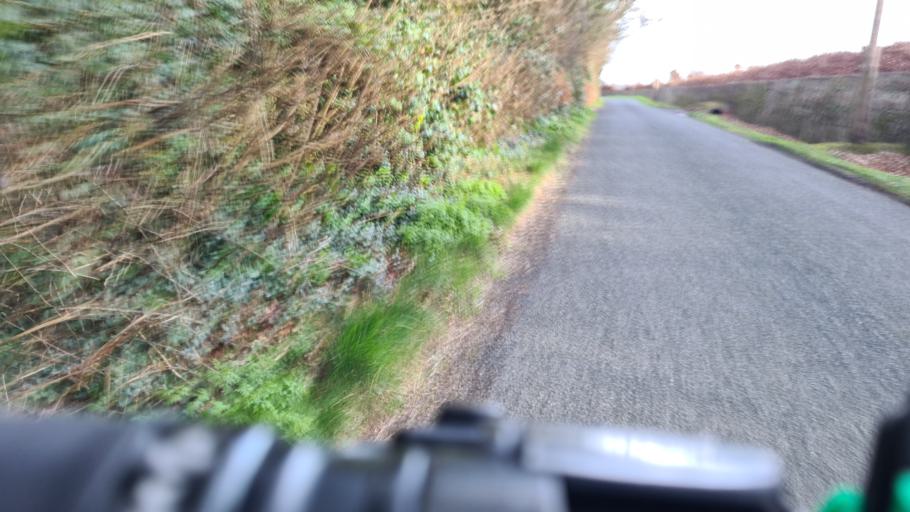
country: IE
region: Leinster
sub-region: Kildare
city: Celbridge
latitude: 53.3373
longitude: -6.5853
